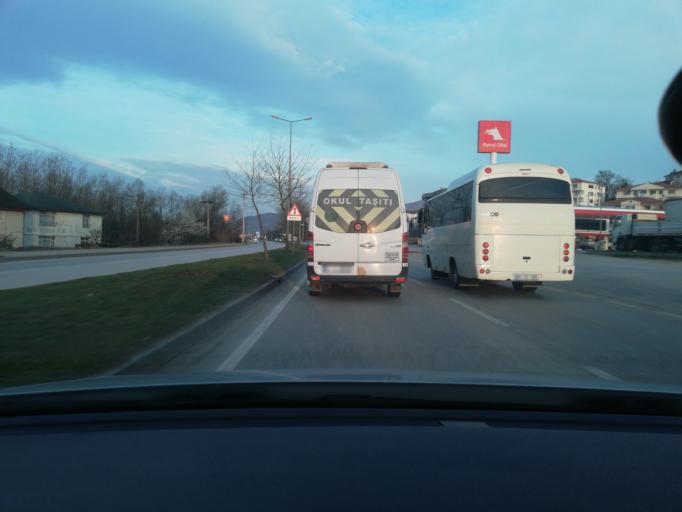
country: TR
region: Duzce
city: Konuralp
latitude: 40.8997
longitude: 31.1599
